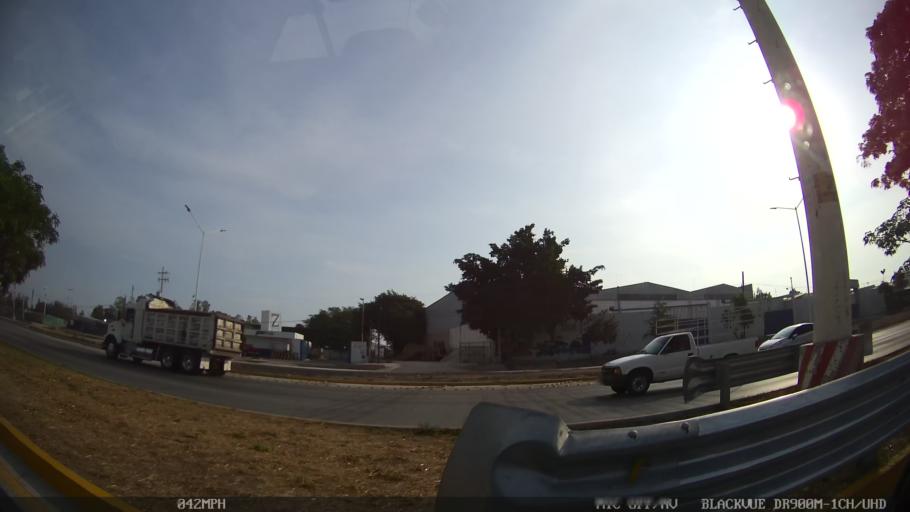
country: MX
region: Jalisco
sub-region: Zapopan
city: Zapopan
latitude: 20.7169
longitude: -103.3086
